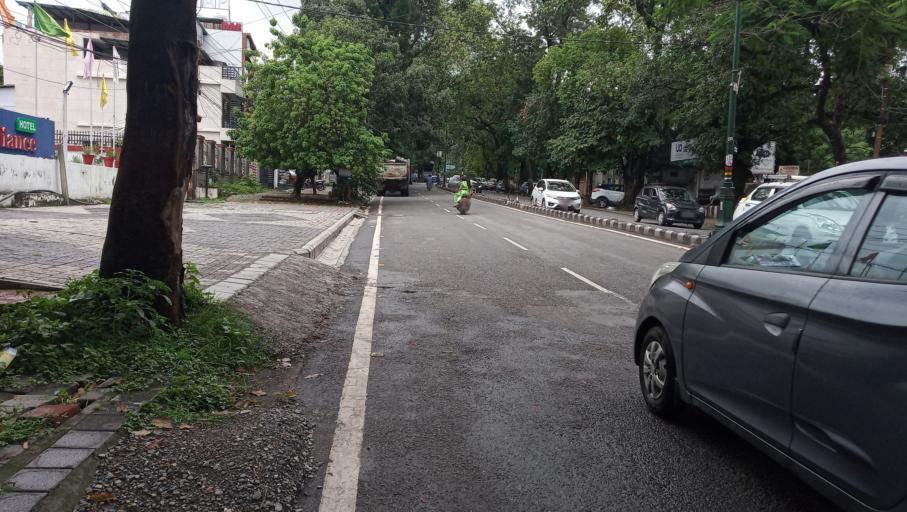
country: IN
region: Uttarakhand
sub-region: Dehradun
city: Dehradun
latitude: 30.3689
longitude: 78.0744
